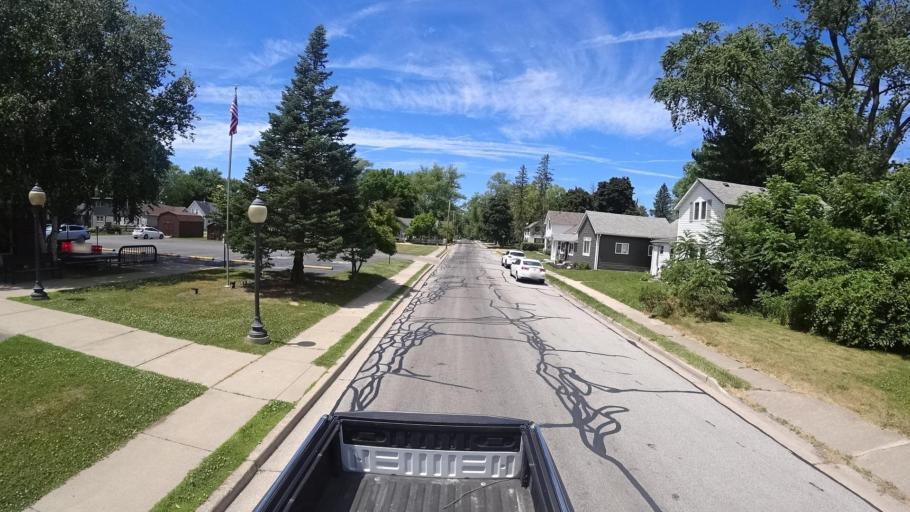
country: US
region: Indiana
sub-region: Porter County
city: Porter
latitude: 41.6165
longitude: -87.0730
